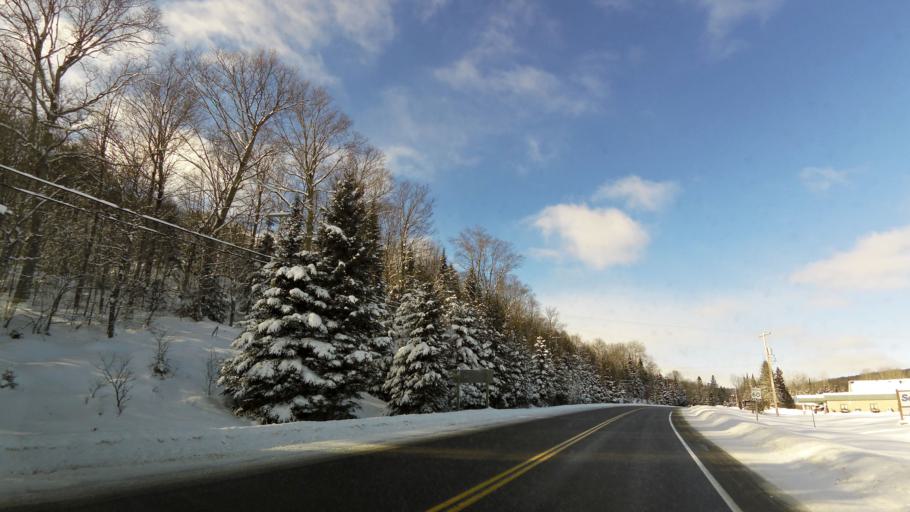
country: CA
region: Ontario
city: Bancroft
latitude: 45.0606
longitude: -78.5209
